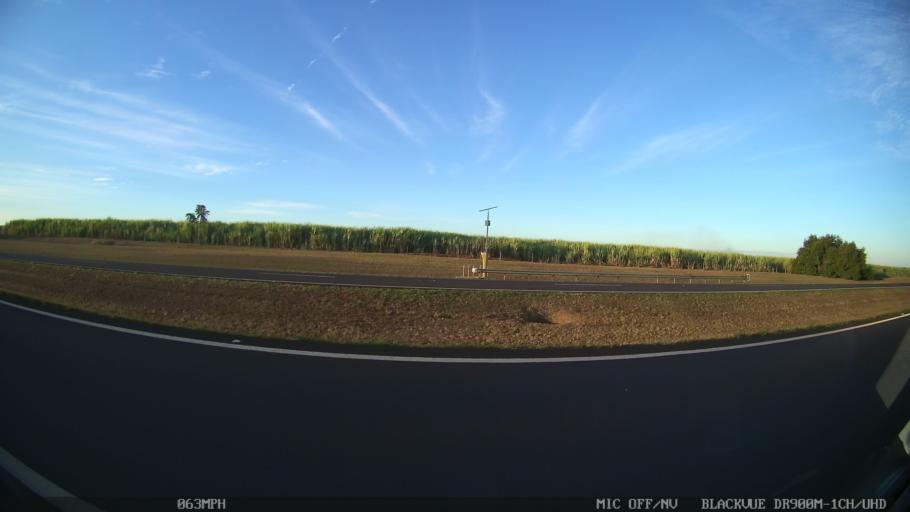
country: BR
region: Sao Paulo
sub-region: Catanduva
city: Catanduva
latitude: -21.1045
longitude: -49.0582
